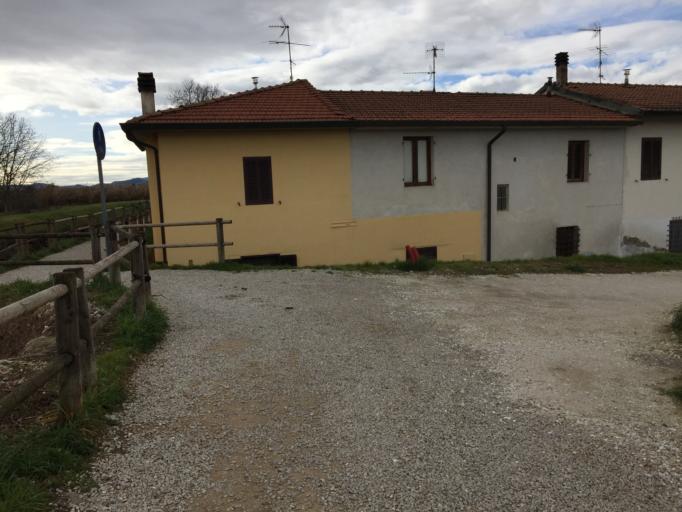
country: IT
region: Tuscany
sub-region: Provincia di Prato
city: Fornacelle
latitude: 43.8841
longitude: 11.0502
